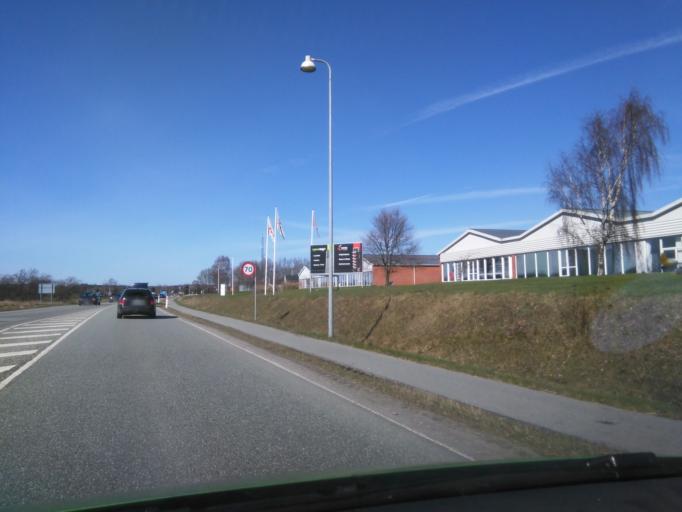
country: DK
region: Central Jutland
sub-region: Favrskov Kommune
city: Hinnerup
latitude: 56.2496
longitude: 10.0706
